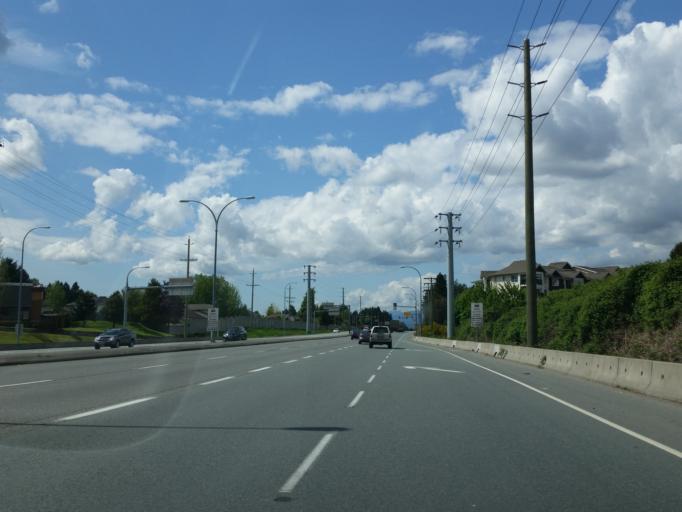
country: CA
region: British Columbia
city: Pitt Meadows
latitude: 49.2244
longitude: -122.6718
